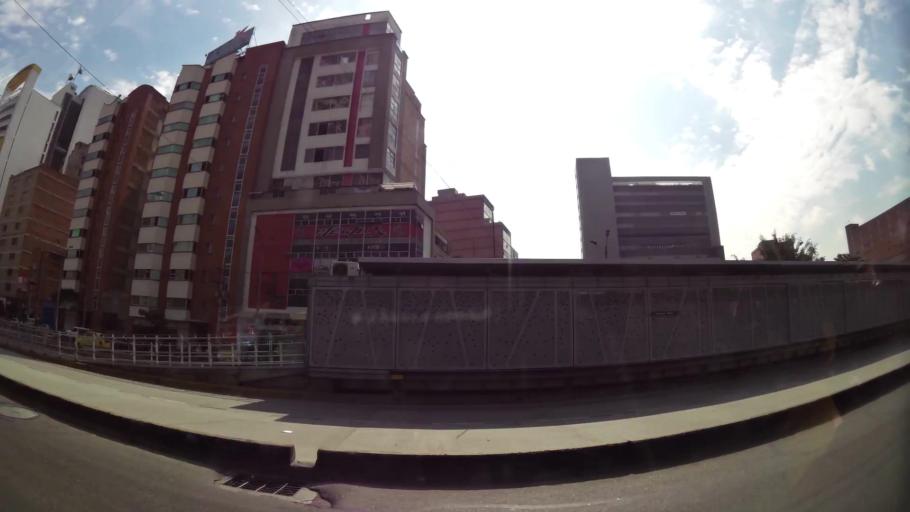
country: CO
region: Antioquia
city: Medellin
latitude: 6.2512
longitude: -75.5751
